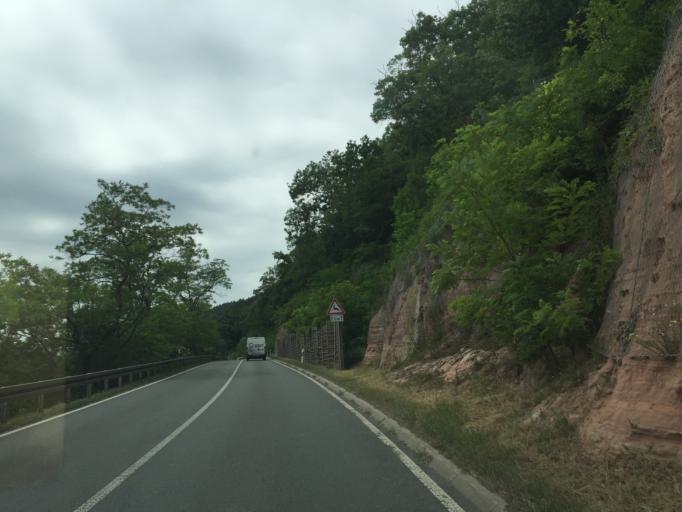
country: DE
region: Thuringia
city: Reinstadt
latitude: 50.7429
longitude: 11.4564
